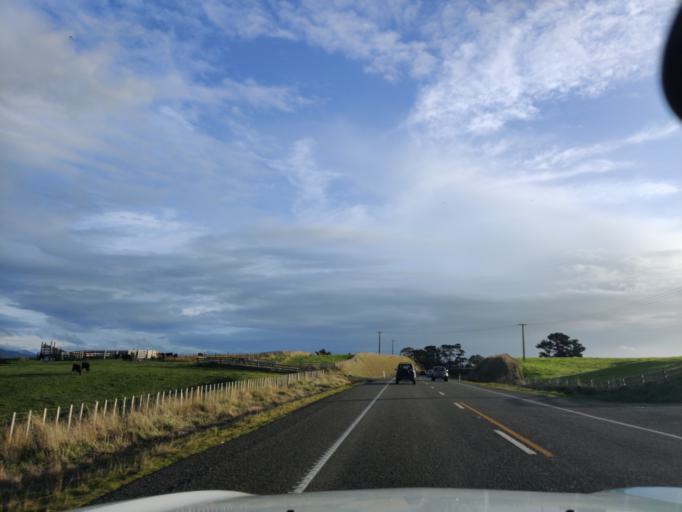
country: NZ
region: Manawatu-Wanganui
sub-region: Horowhenua District
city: Foxton
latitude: -40.5115
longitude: 175.4672
